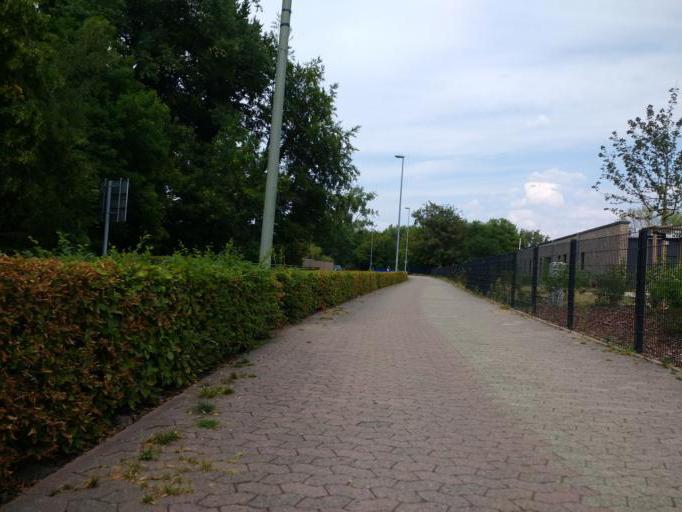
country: DE
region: Lower Saxony
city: Gifhorn
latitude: 52.4831
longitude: 10.5520
